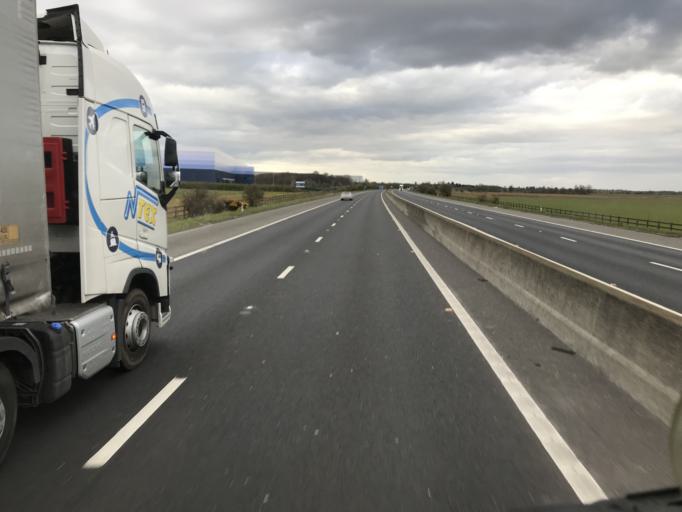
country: GB
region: England
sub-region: Doncaster
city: Armthorpe
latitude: 53.5239
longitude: -1.0390
